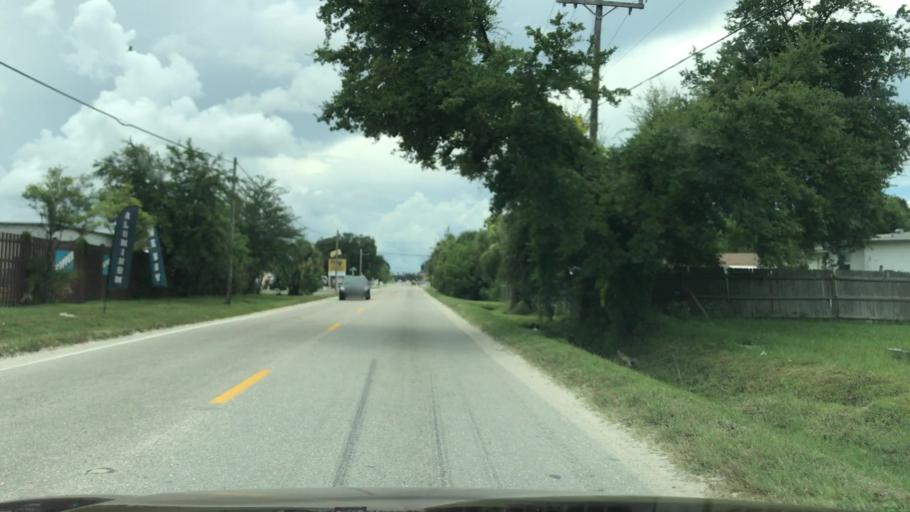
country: US
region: Florida
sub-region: Sarasota County
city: North Sarasota
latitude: 27.3671
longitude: -82.5365
